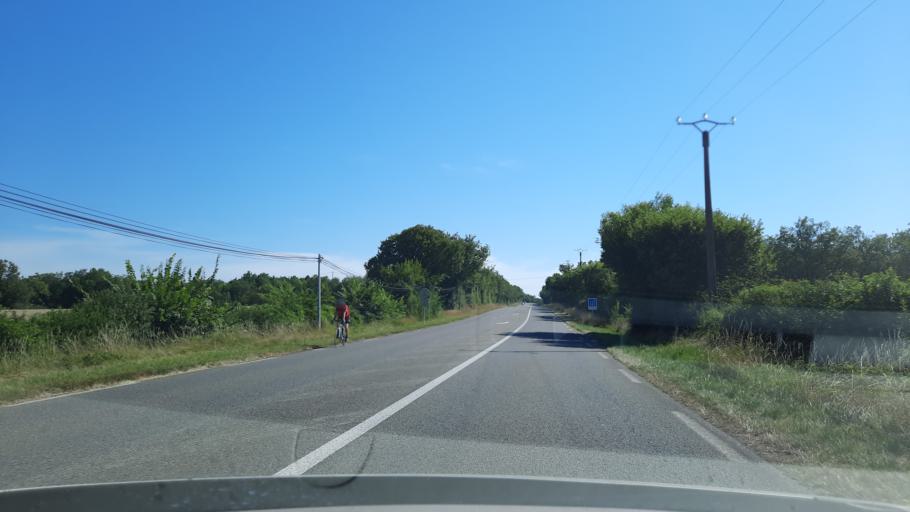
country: FR
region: Midi-Pyrenees
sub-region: Departement du Tarn-et-Garonne
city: Caylus
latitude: 44.2220
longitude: 1.7425
